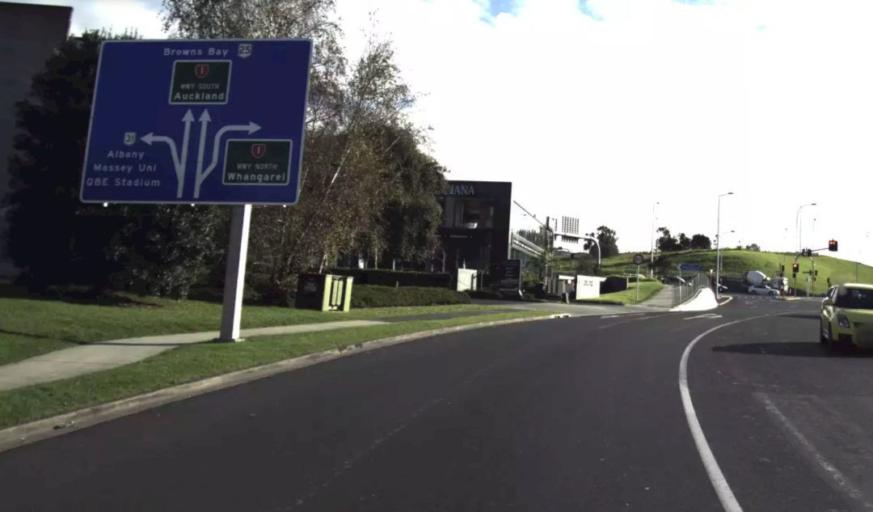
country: NZ
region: Auckland
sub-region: Auckland
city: Rothesay Bay
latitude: -36.7369
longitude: 174.7162
